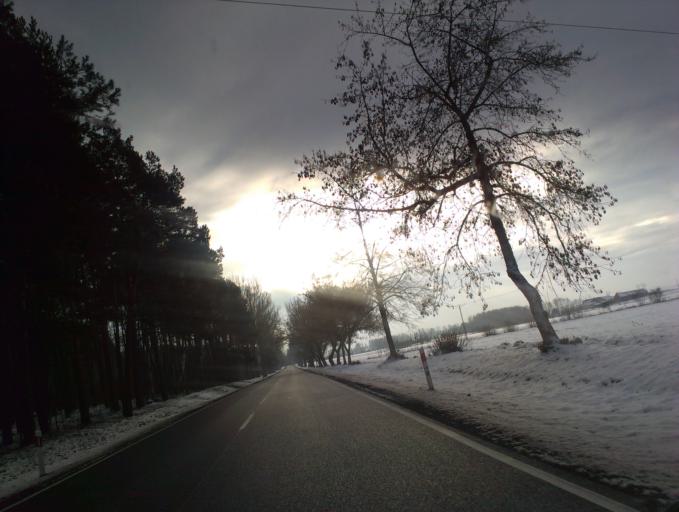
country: PL
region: Greater Poland Voivodeship
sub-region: Powiat zlotowski
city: Okonek
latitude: 53.4957
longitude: 16.8595
